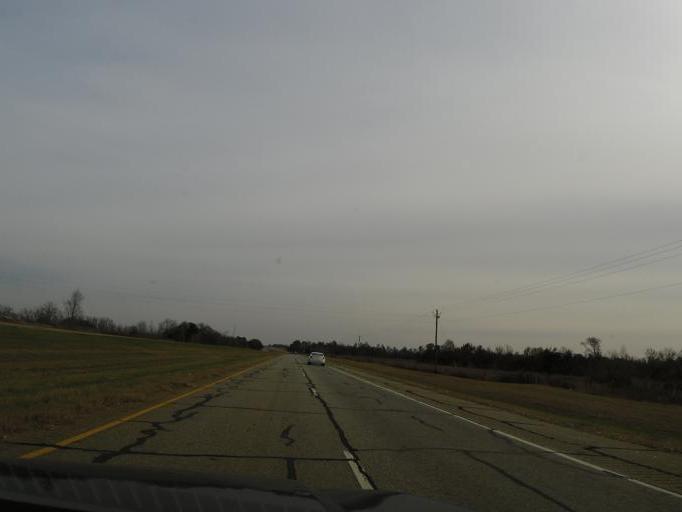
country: US
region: Georgia
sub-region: Seminole County
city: Donalsonville
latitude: 31.0693
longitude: -84.9470
